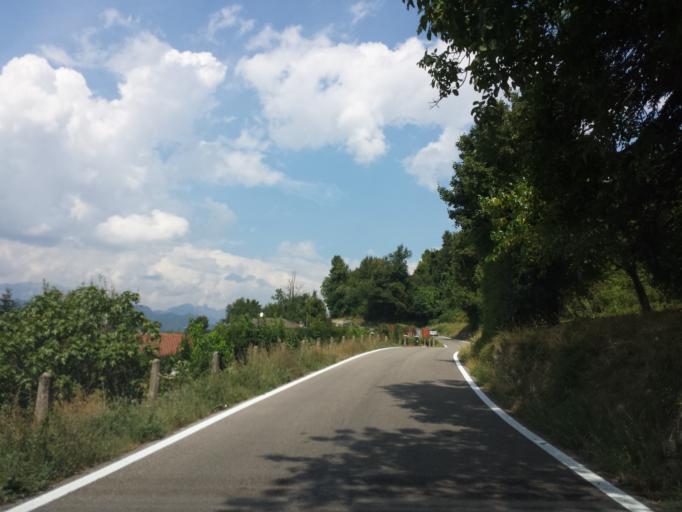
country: IT
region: Veneto
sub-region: Provincia di Vicenza
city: Valdagno
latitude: 45.6388
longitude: 11.3187
